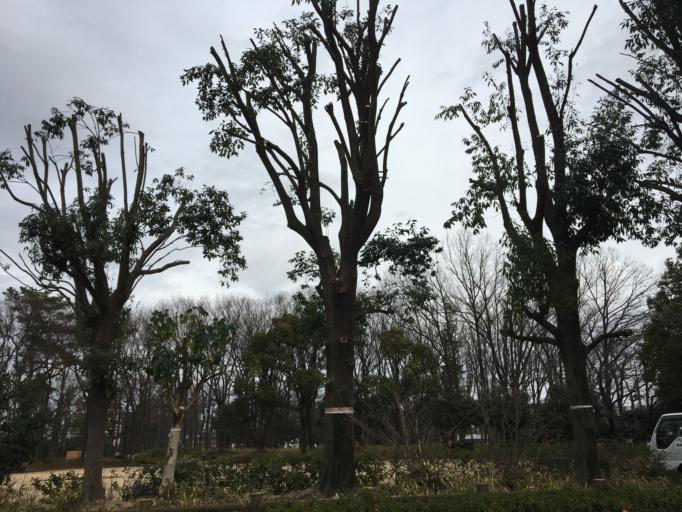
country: JP
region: Saitama
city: Tokorozawa
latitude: 35.7973
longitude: 139.5088
